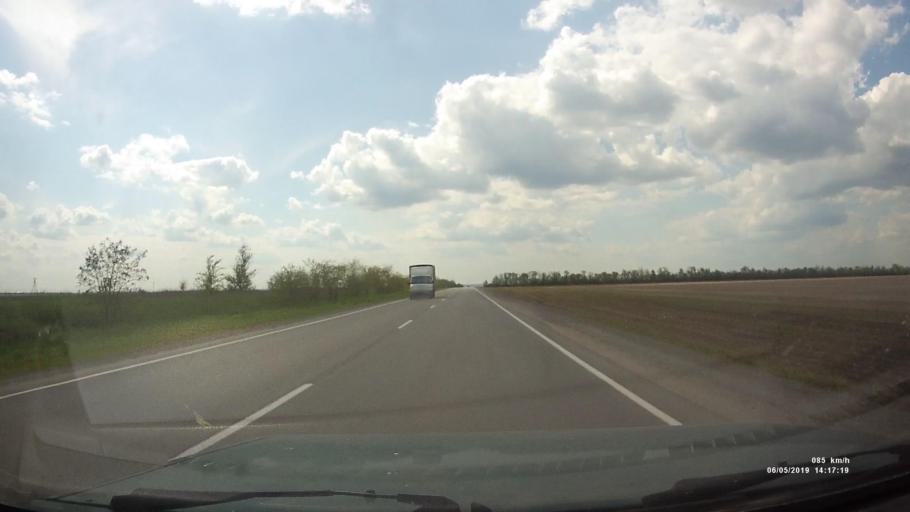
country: RU
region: Rostov
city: Kamenolomni
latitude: 47.6342
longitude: 40.2707
